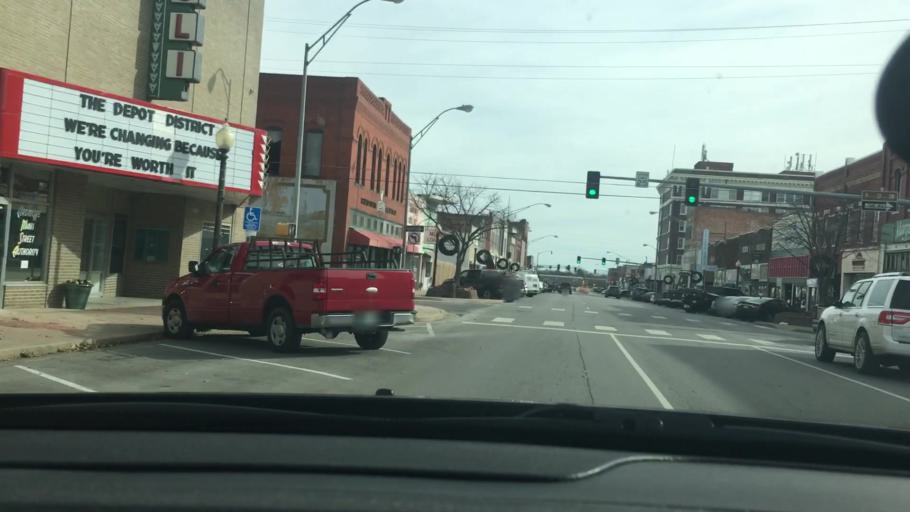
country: US
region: Oklahoma
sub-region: Carter County
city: Ardmore
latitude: 34.1732
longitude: -97.1309
